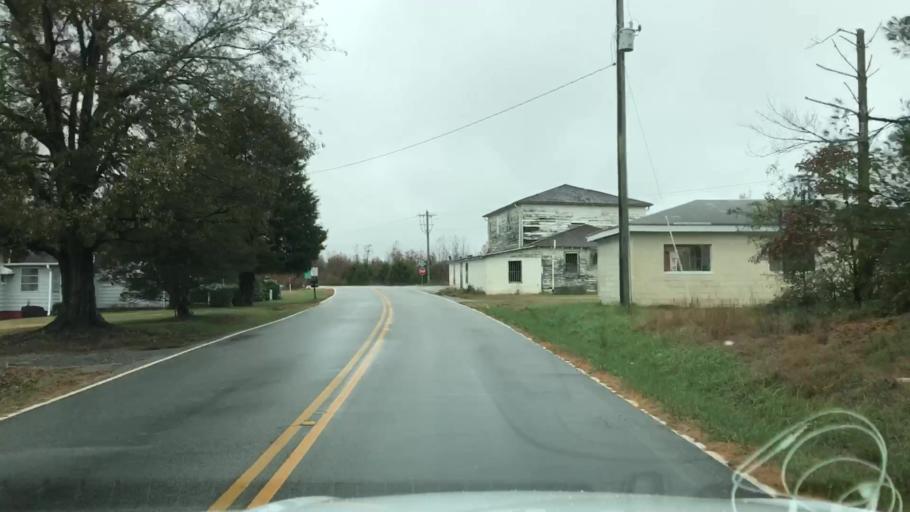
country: US
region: South Carolina
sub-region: Spartanburg County
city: Roebuck
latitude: 34.7936
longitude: -81.9142
